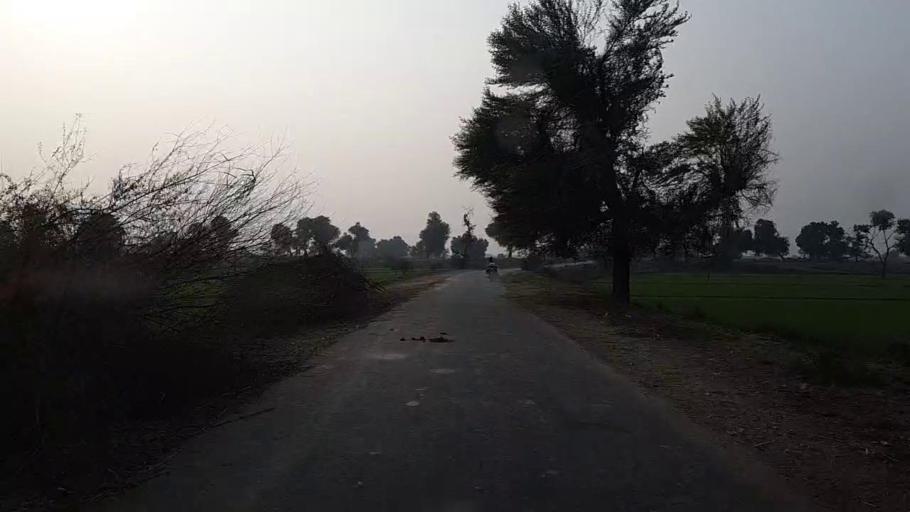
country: PK
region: Sindh
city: Setharja Old
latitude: 27.0812
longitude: 68.5060
